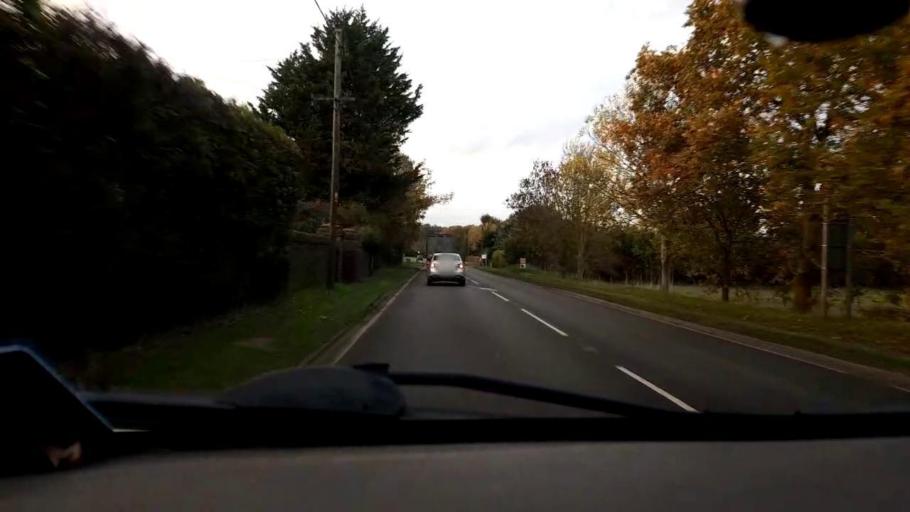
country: GB
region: England
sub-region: Norfolk
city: Costessey
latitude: 52.7097
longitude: 1.1415
